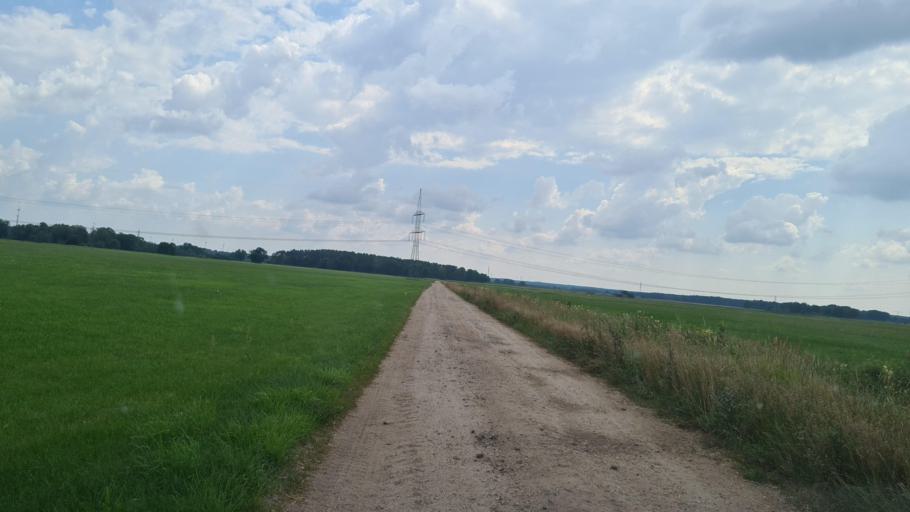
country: DE
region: Brandenburg
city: Sallgast
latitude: 51.6328
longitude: 13.8672
